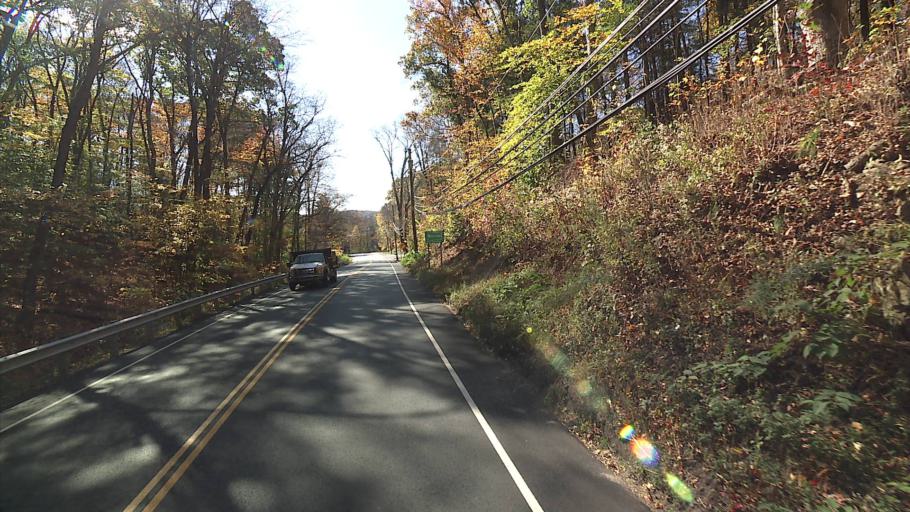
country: US
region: Connecticut
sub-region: Litchfield County
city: Watertown
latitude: 41.6145
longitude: -73.1115
